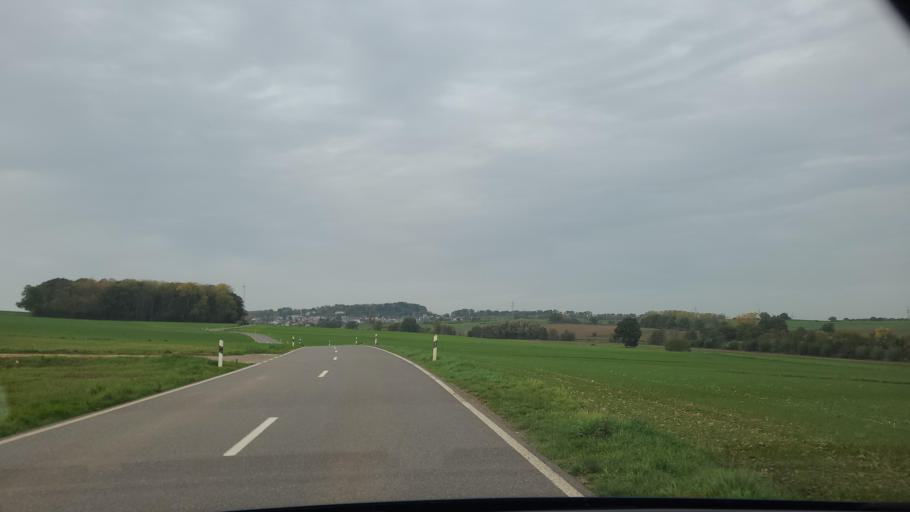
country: LU
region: Luxembourg
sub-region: Canton de Capellen
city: Dippach
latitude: 49.6130
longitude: 5.9791
